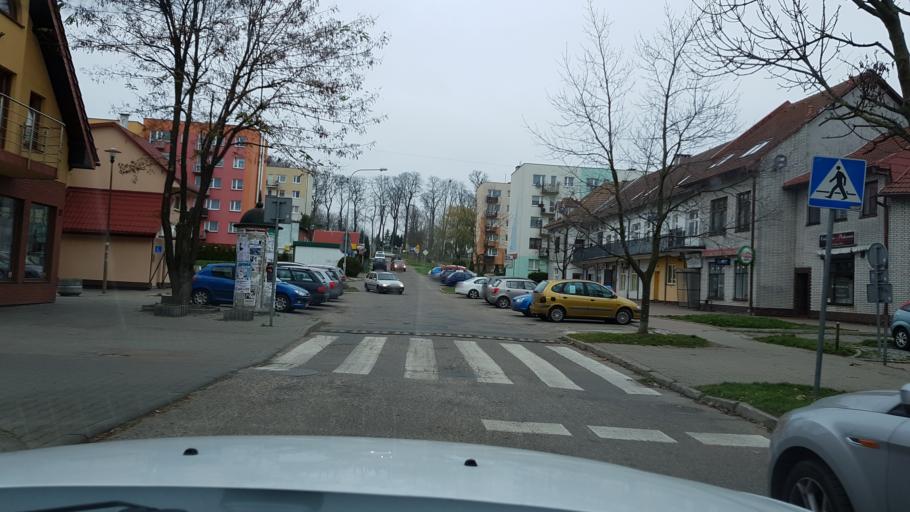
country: PL
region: West Pomeranian Voivodeship
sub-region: Powiat slawienski
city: Darlowo
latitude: 54.4223
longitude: 16.4171
